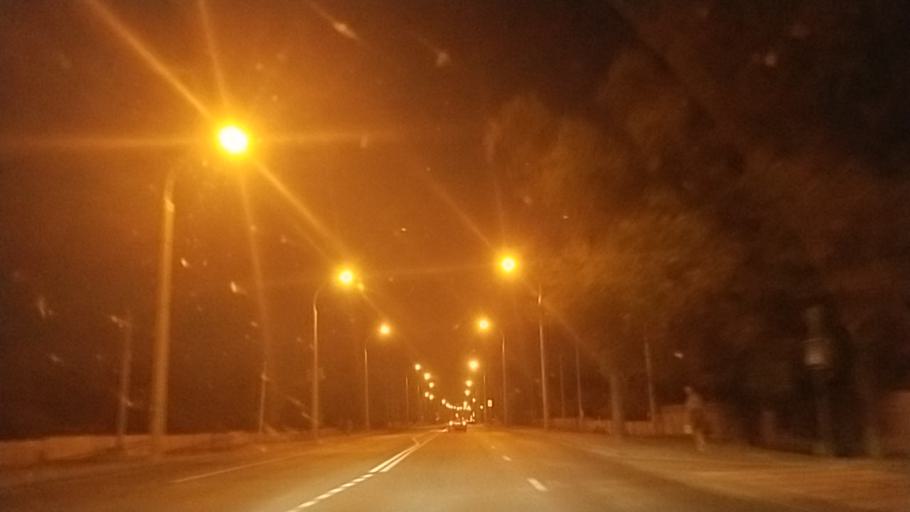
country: BY
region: Brest
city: Brest
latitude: 52.0639
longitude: 23.7365
